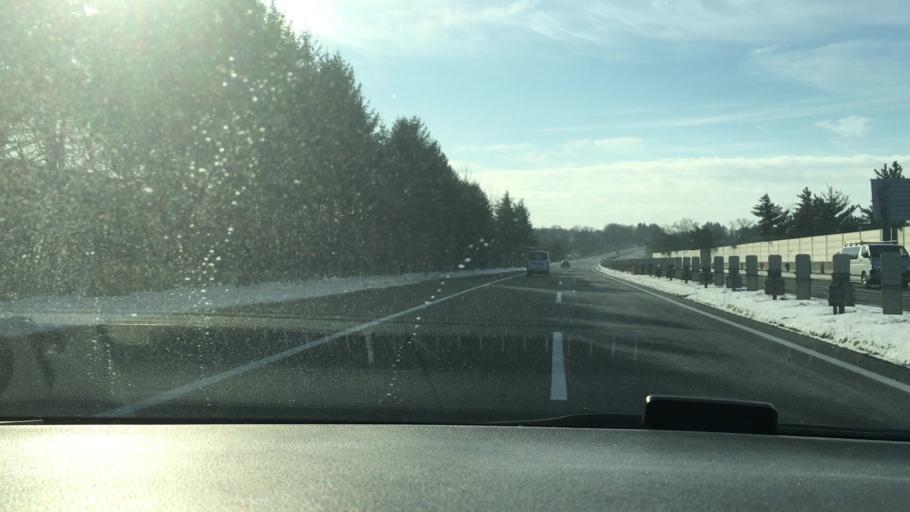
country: JP
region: Iwate
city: Hanamaki
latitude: 39.3792
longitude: 141.0927
